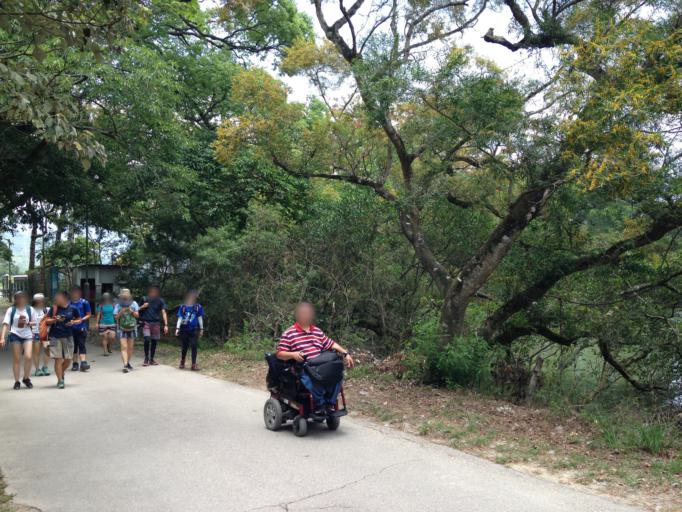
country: CN
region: Guangdong
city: Haishan
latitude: 22.5238
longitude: 114.2084
